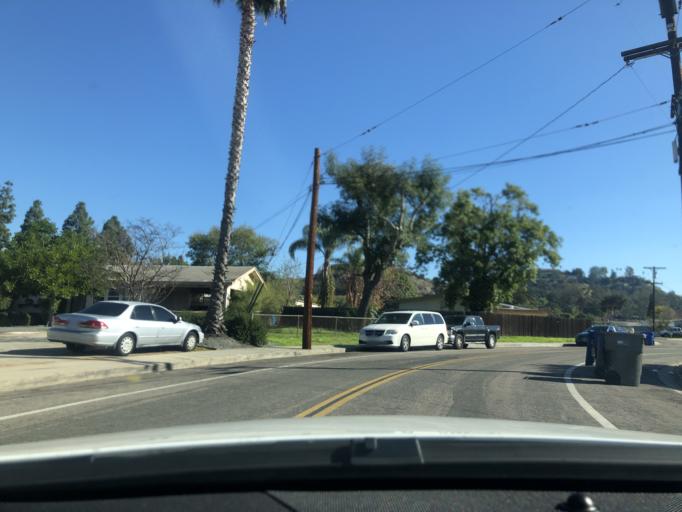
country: US
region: California
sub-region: San Diego County
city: El Cajon
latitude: 32.7839
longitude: -116.9507
